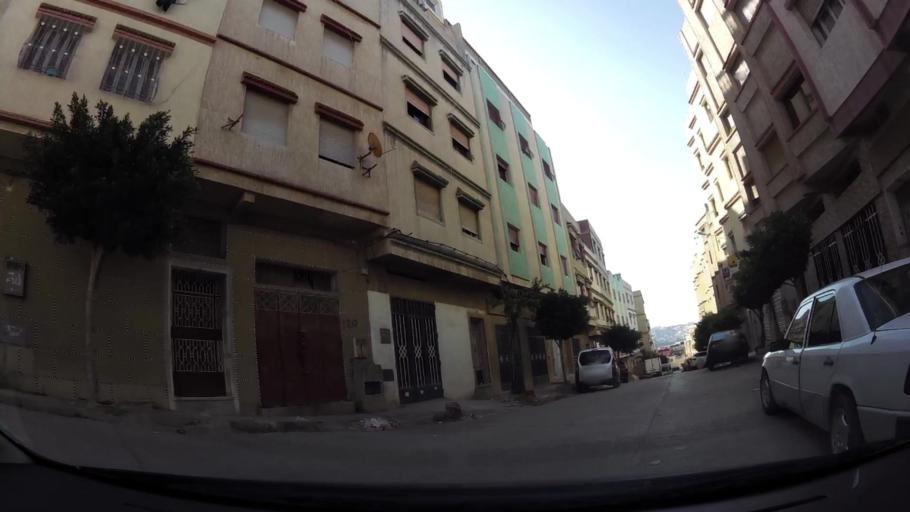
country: MA
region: Tanger-Tetouan
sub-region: Tanger-Assilah
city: Tangier
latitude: 35.7636
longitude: -5.7920
